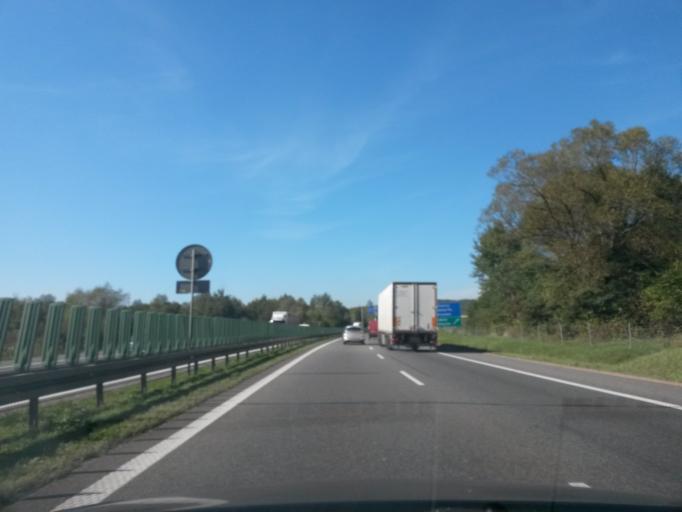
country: PL
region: Lesser Poland Voivodeship
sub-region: Krakow
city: Sidzina
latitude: 49.9954
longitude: 19.8608
